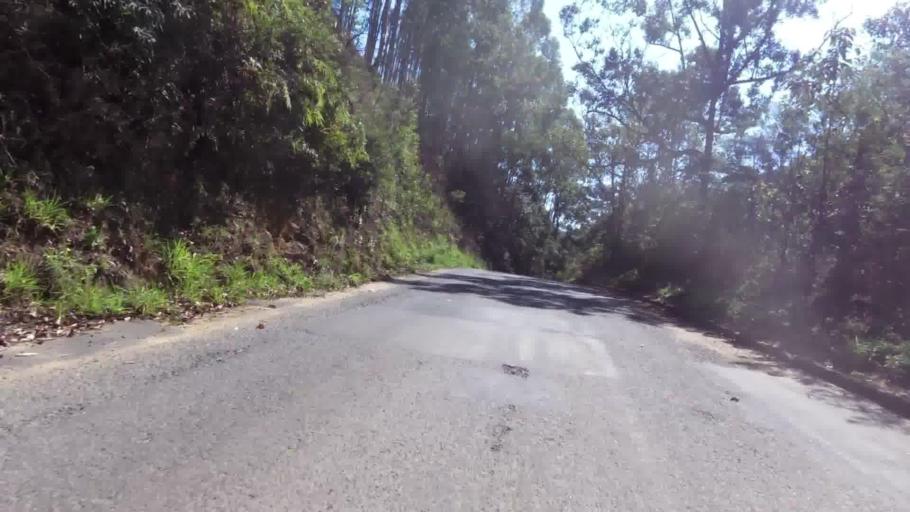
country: BR
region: Espirito Santo
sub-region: Marechal Floriano
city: Marechal Floriano
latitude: -20.4558
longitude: -40.9041
